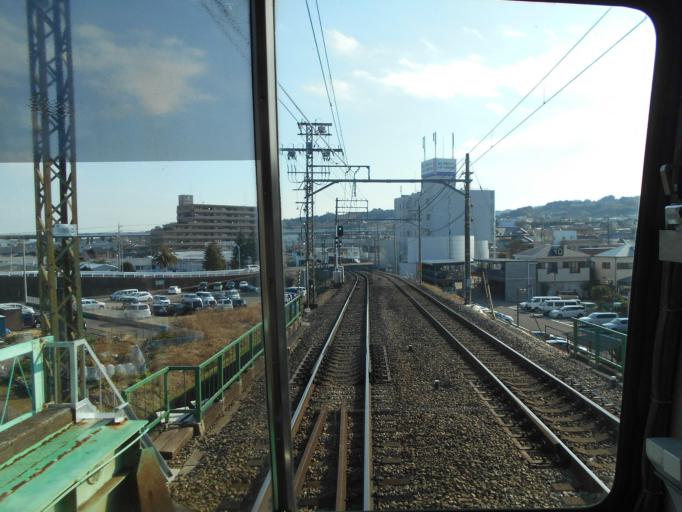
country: JP
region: Shizuoka
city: Shizuoka-shi
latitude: 34.9935
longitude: 138.4278
